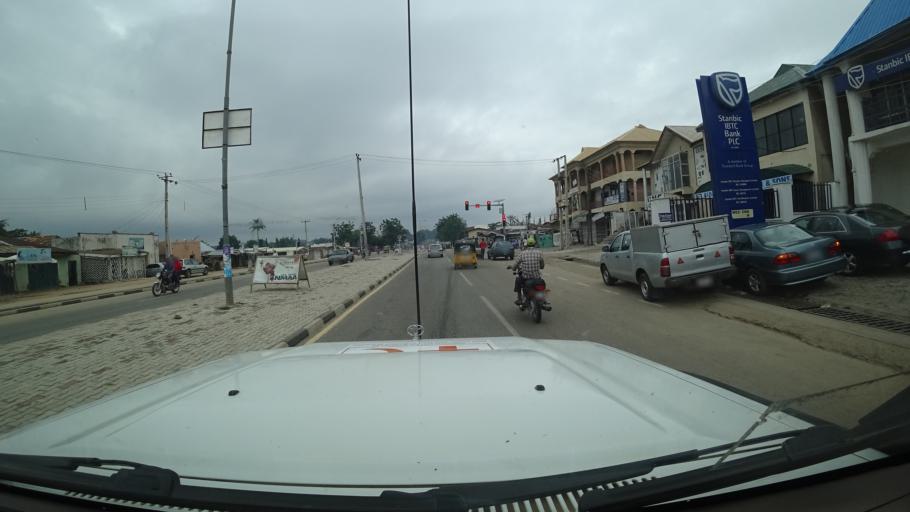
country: NG
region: Niger
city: Minna
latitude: 9.6208
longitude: 6.5460
